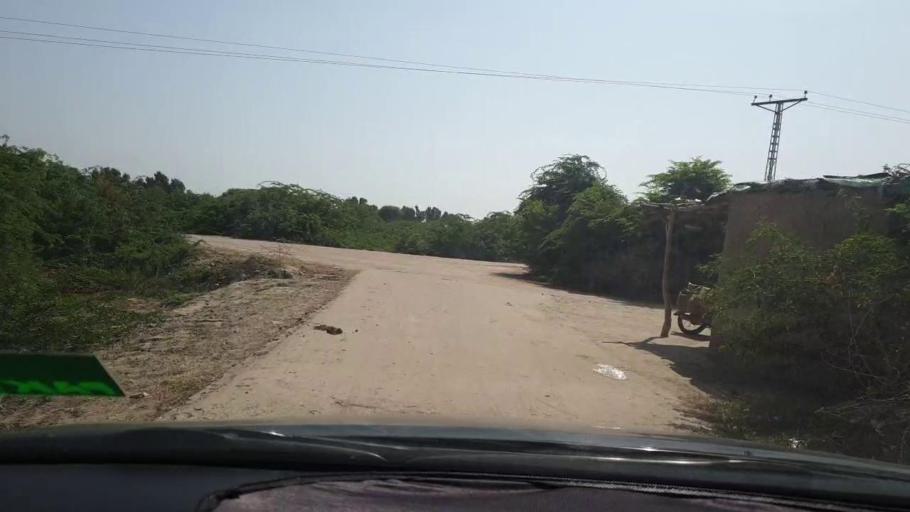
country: PK
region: Sindh
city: Naukot
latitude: 24.9354
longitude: 69.1876
